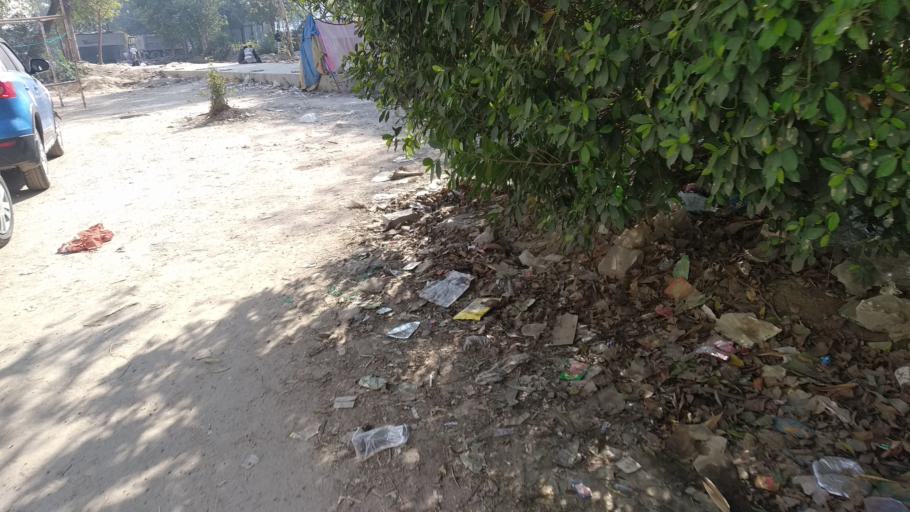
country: IN
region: NCT
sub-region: New Delhi
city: New Delhi
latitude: 28.6180
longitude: 77.2406
